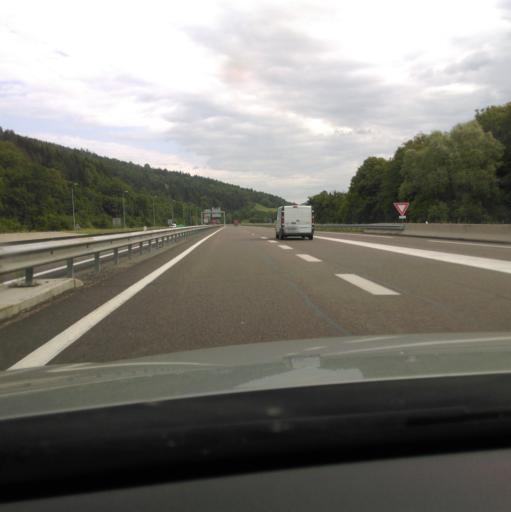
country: FR
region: Rhone-Alpes
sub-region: Departement de l'Ain
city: Saint-Martin-du-Frene
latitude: 46.1380
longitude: 5.5415
